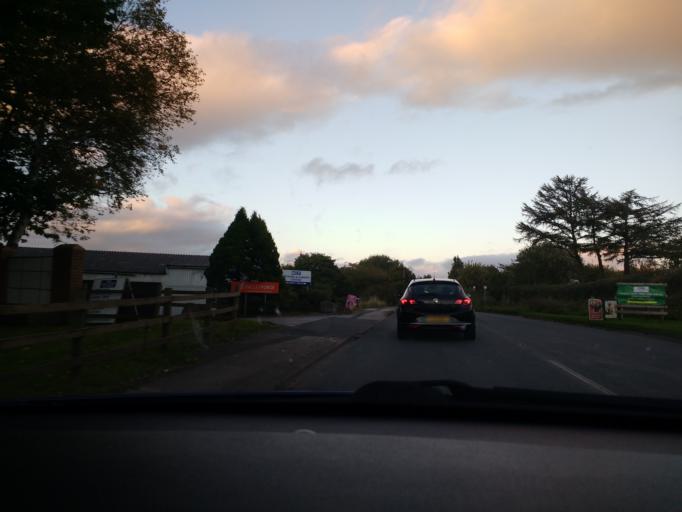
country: GB
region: England
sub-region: Lancashire
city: Caton
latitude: 54.0915
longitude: -2.6693
